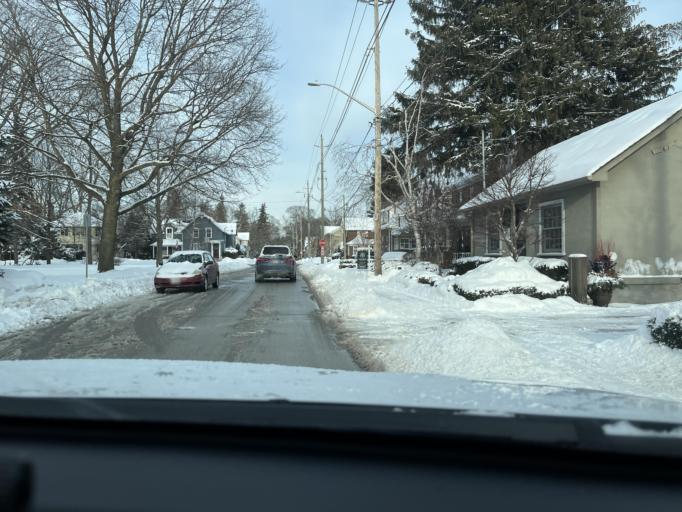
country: CA
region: Ontario
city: Oakville
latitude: 43.4492
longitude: -79.6689
